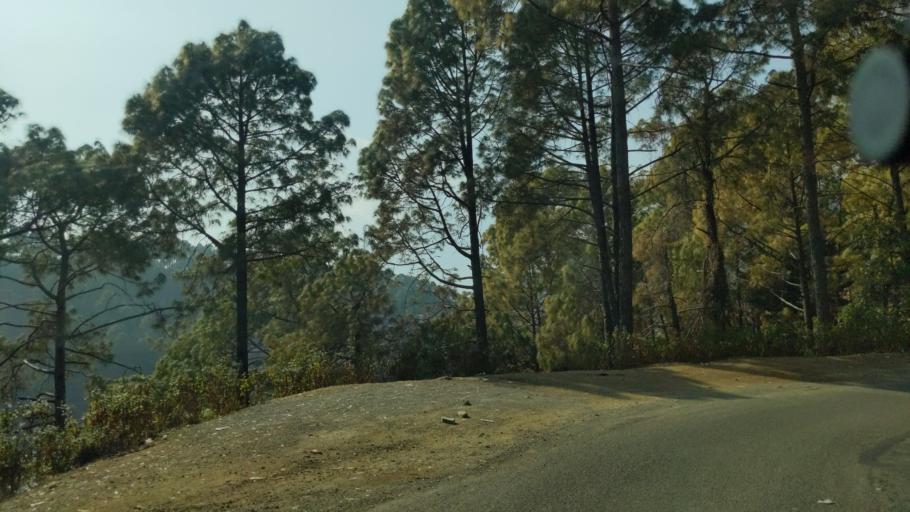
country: IN
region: Uttarakhand
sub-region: Naini Tal
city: Bhowali
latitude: 29.3888
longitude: 79.5400
